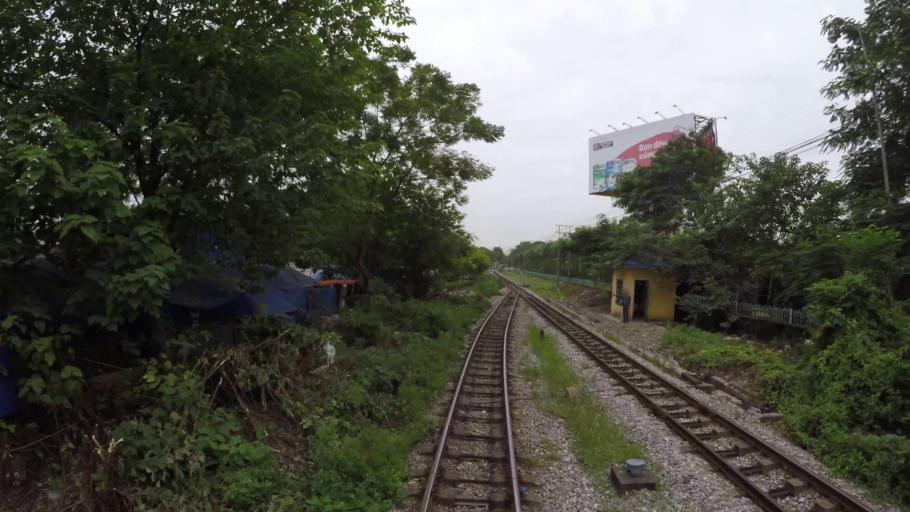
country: VN
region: Hai Phong
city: An Duong
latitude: 20.8774
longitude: 106.6311
